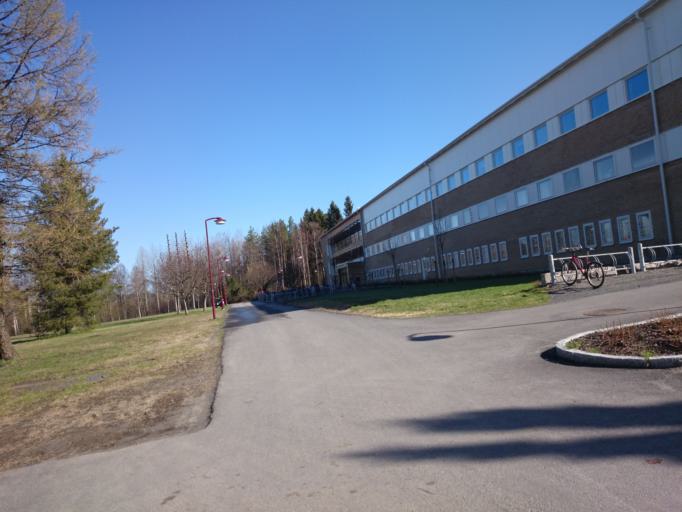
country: SE
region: Vaesterbotten
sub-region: Umea Kommun
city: Umea
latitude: 63.8201
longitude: 20.3123
